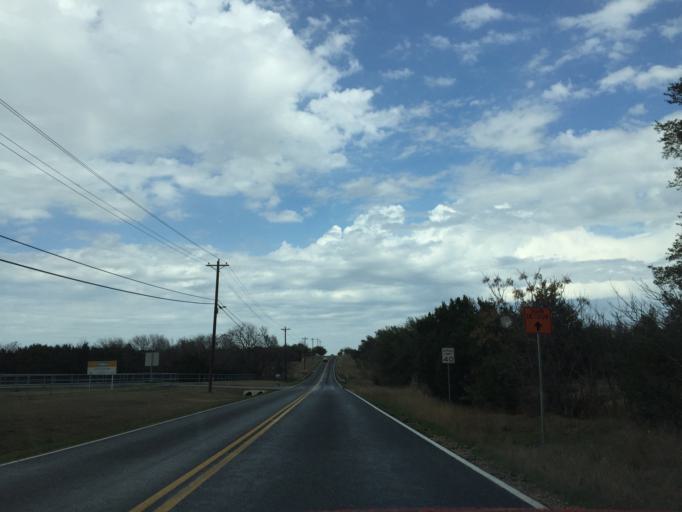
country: US
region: Texas
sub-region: Burnet County
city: Bertram
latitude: 30.6991
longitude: -97.9315
